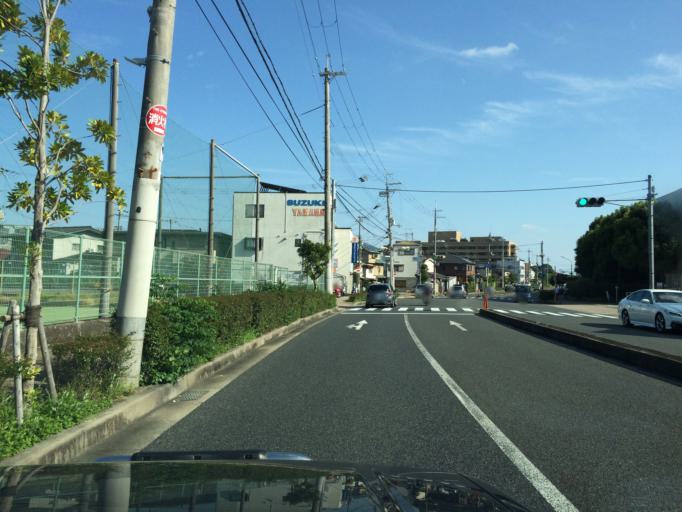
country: JP
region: Hyogo
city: Itami
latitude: 34.7865
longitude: 135.3937
